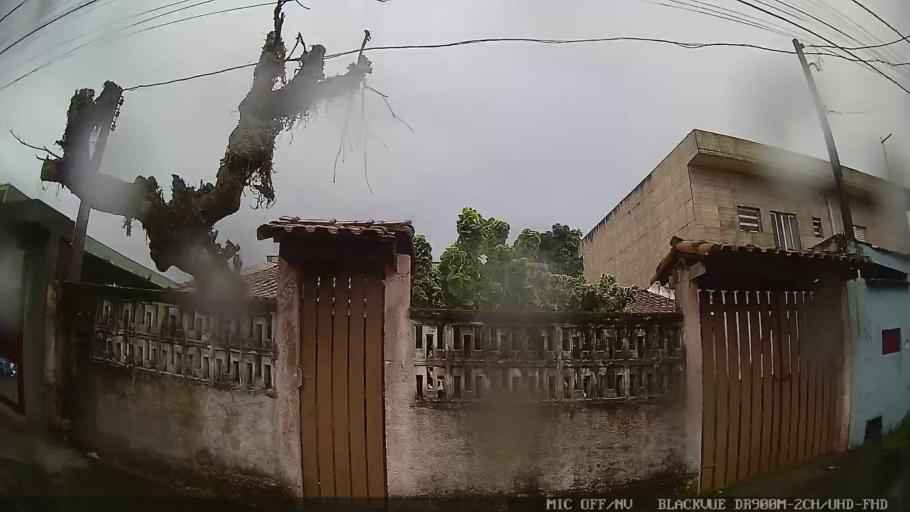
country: BR
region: Sao Paulo
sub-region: Itanhaem
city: Itanhaem
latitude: -24.1673
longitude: -46.7626
